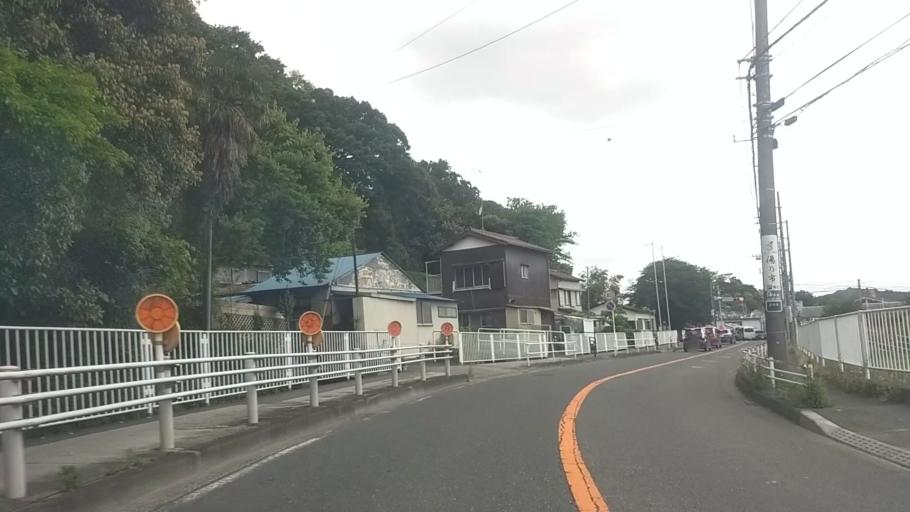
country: JP
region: Kanagawa
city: Fujisawa
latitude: 35.3679
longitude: 139.5224
